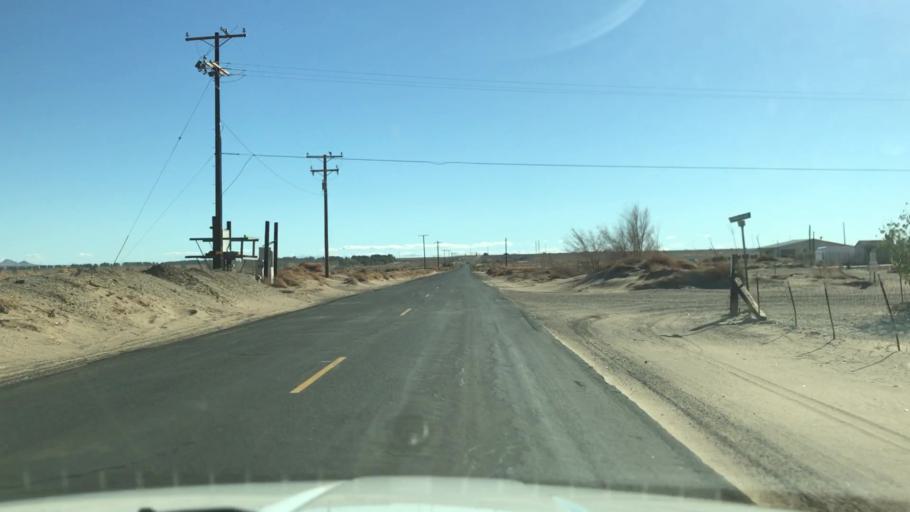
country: US
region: California
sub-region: Kern County
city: California City
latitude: 35.2815
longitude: -117.9858
